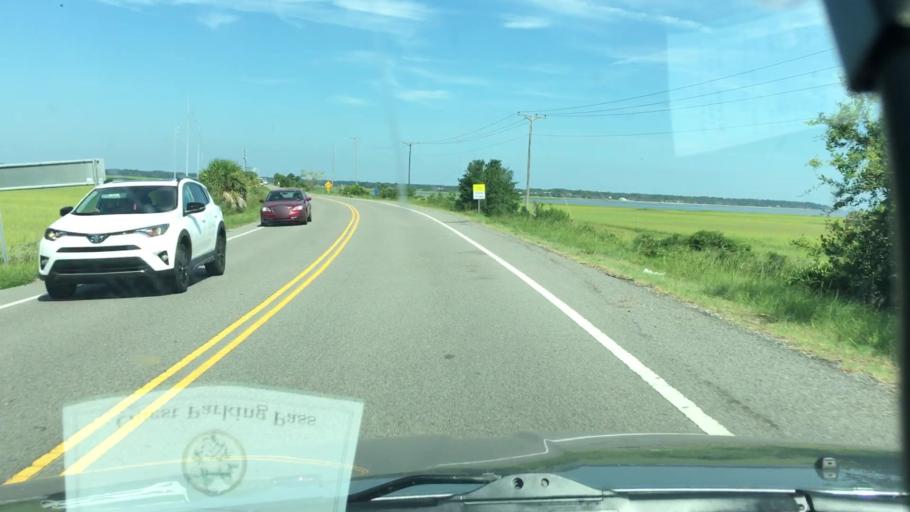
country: US
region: South Carolina
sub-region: Beaufort County
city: Beaufort
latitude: 32.4018
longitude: -80.4461
